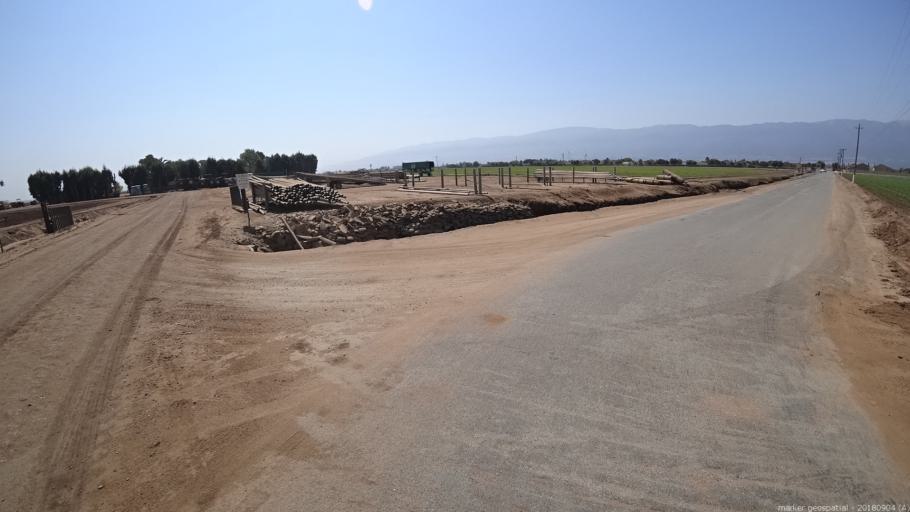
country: US
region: California
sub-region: Monterey County
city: Gonzales
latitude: 36.5278
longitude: -121.4428
